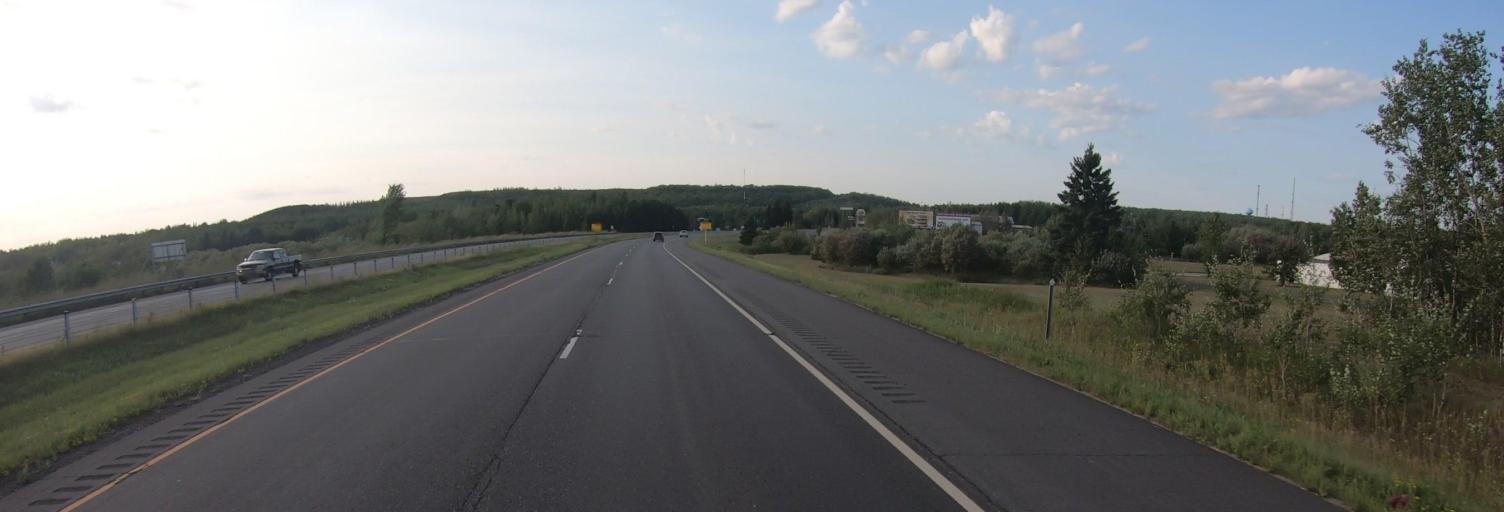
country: US
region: Minnesota
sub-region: Saint Louis County
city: Eveleth
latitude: 47.4742
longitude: -92.5284
